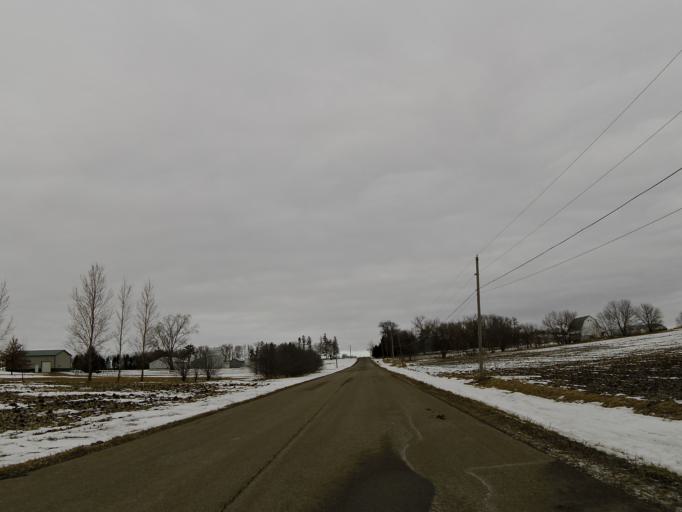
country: US
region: Minnesota
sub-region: Dakota County
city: Hastings
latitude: 44.7956
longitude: -92.8424
